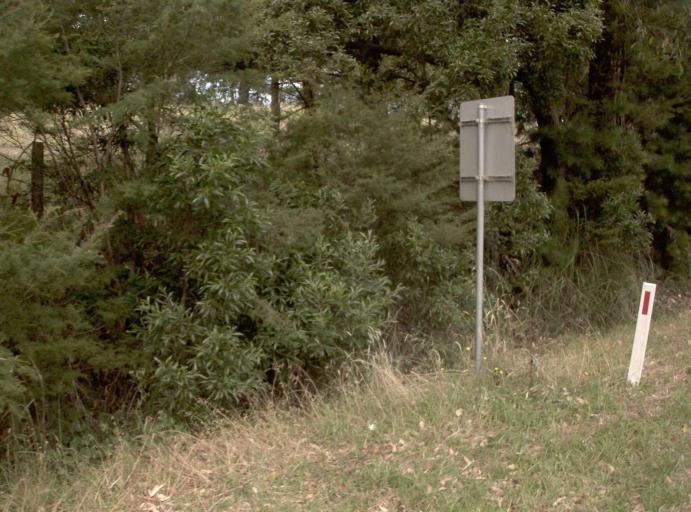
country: AU
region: Victoria
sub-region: Latrobe
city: Traralgon
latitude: -38.1330
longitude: 146.4727
